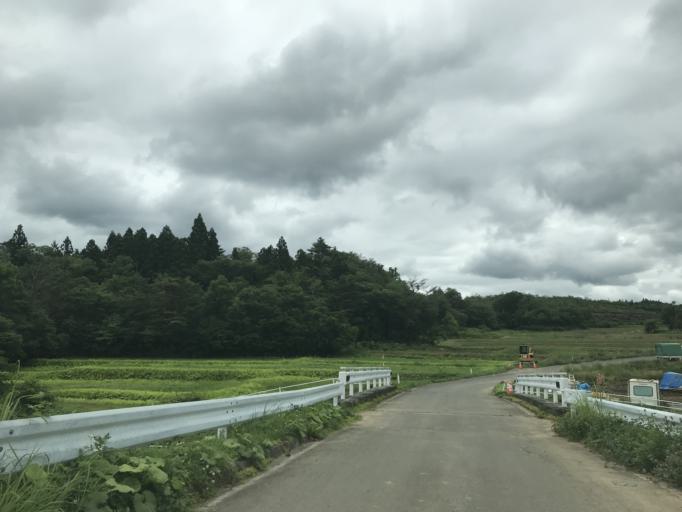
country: JP
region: Iwate
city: Ichinoseki
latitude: 38.9121
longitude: 141.0149
